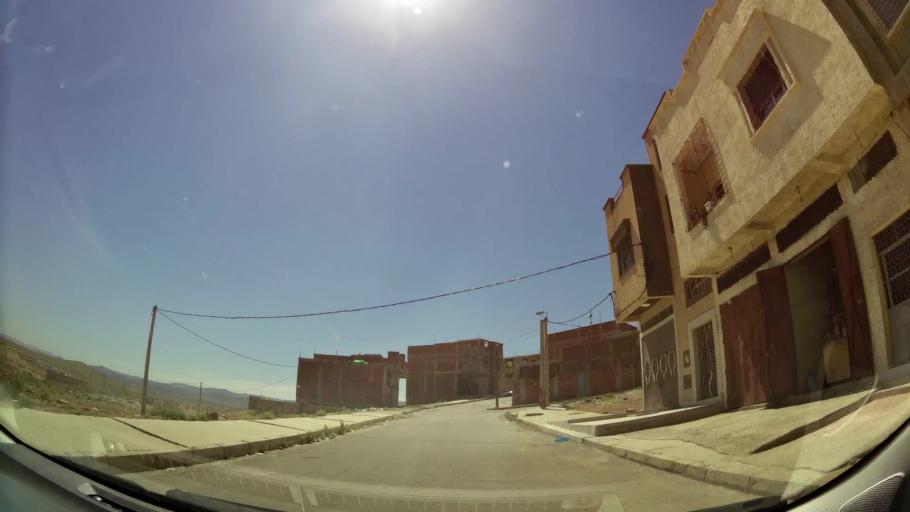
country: MA
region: Oriental
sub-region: Oujda-Angad
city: Oujda
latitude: 34.6500
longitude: -1.8733
